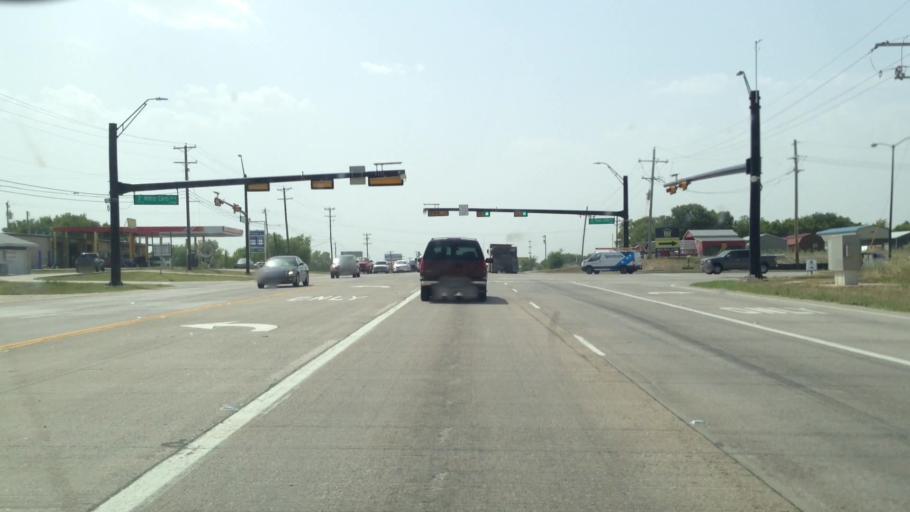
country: US
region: Texas
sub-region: Collin County
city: Lowry Crossing
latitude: 33.1848
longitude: -96.5369
